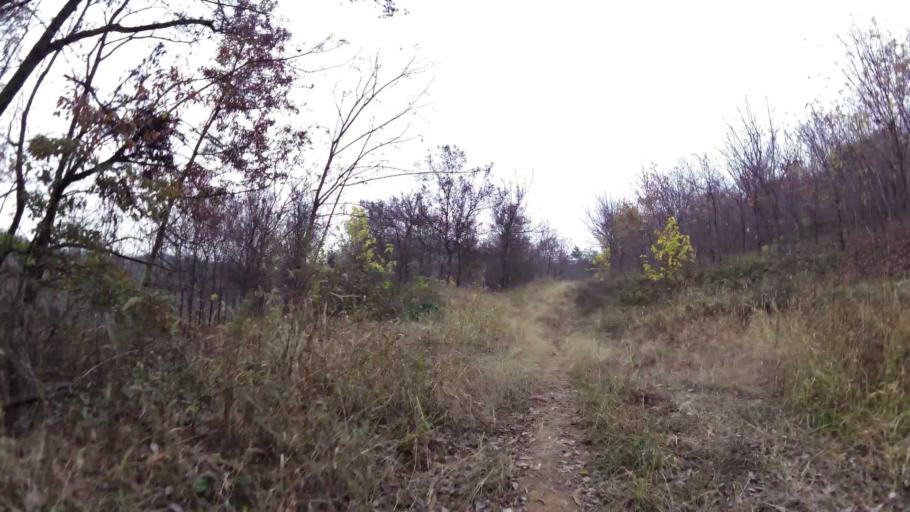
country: KR
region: Daegu
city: Daegu
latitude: 35.8569
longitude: 128.6530
